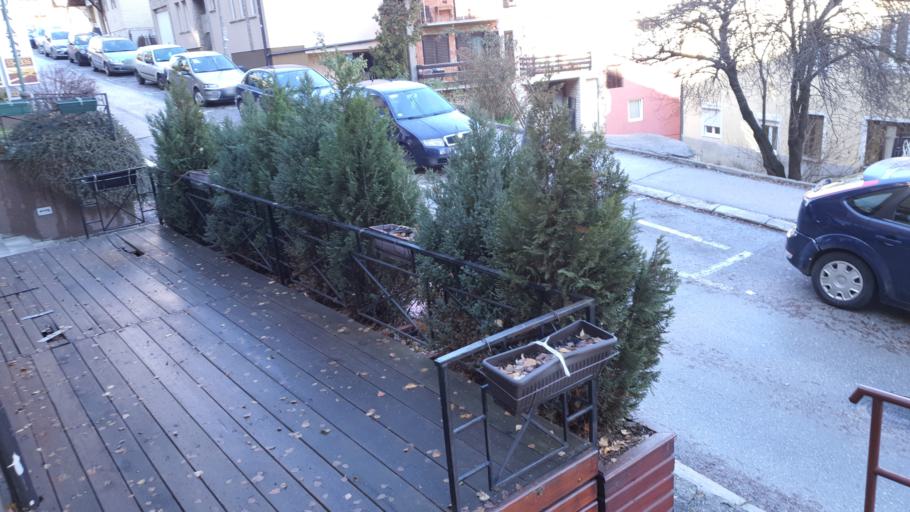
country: RS
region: Central Serbia
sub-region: Zlatiborski Okrug
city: Uzice
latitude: 43.8561
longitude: 19.8331
